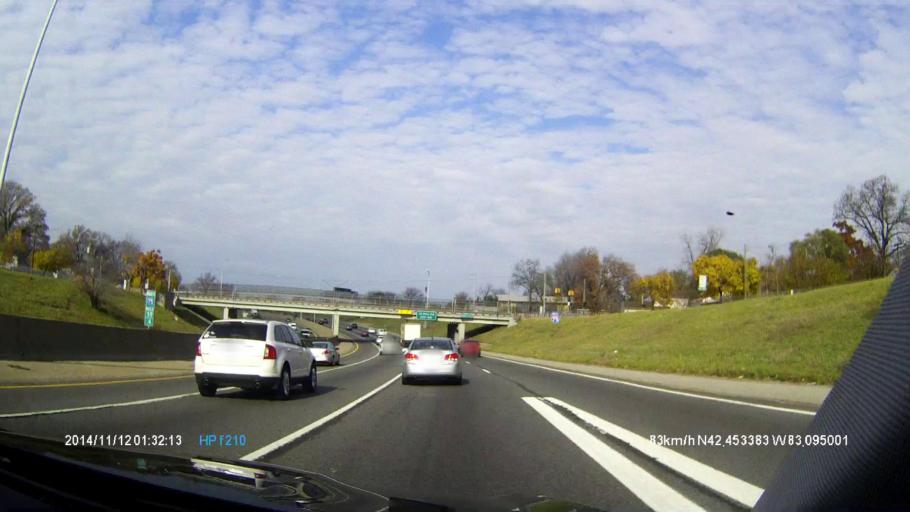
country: US
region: Michigan
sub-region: Oakland County
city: Hazel Park
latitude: 42.4537
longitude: -83.0953
